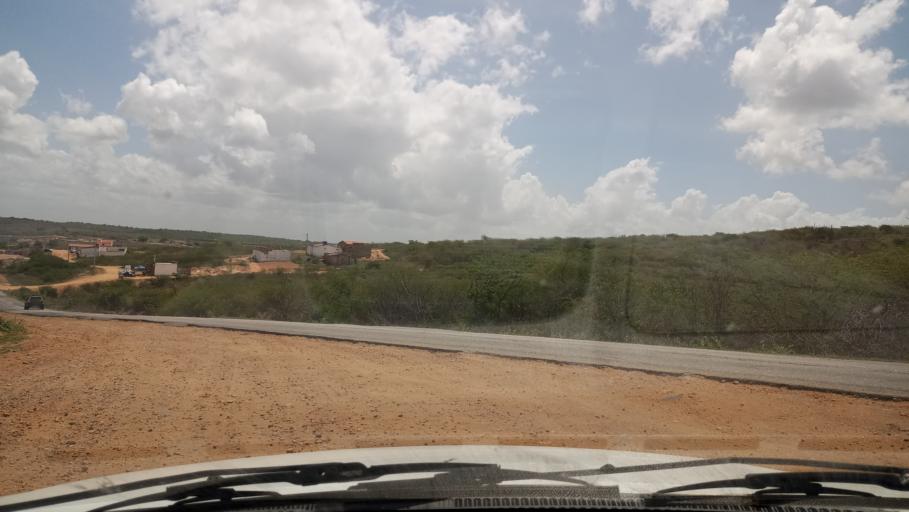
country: BR
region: Rio Grande do Norte
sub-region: Sao Paulo Do Potengi
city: Sao Paulo do Potengi
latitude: -5.9052
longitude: -35.7605
